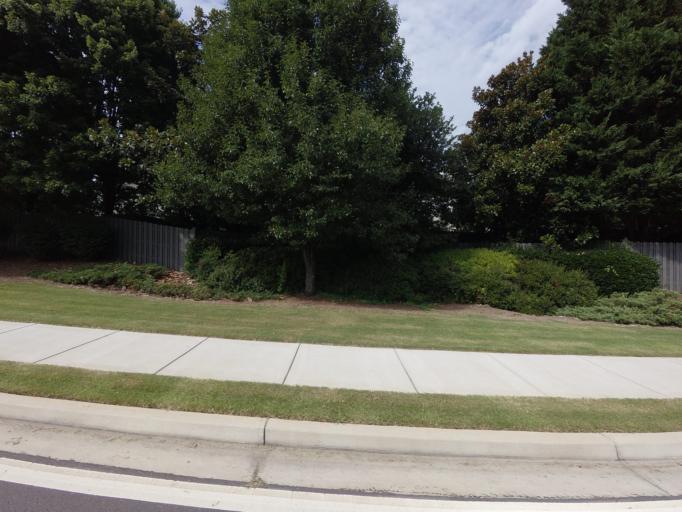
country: US
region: Georgia
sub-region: Fulton County
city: Johns Creek
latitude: 34.0469
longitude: -84.1695
